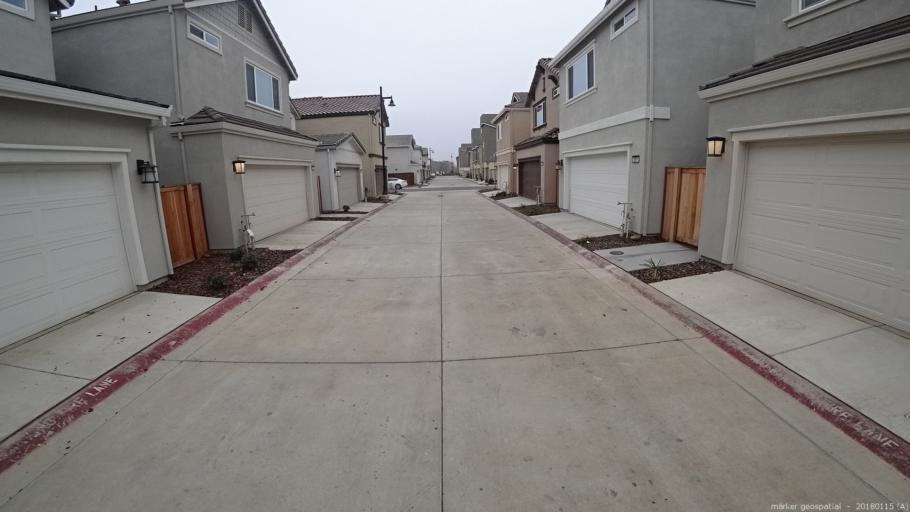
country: US
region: California
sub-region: Sacramento County
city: Rancho Cordova
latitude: 38.5812
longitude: -121.2809
